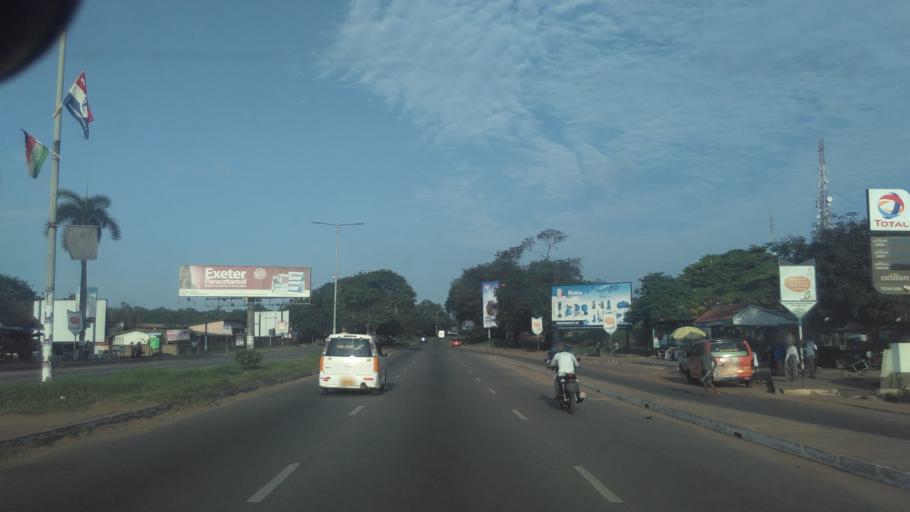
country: GH
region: Greater Accra
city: Accra
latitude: 5.5738
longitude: -0.1981
